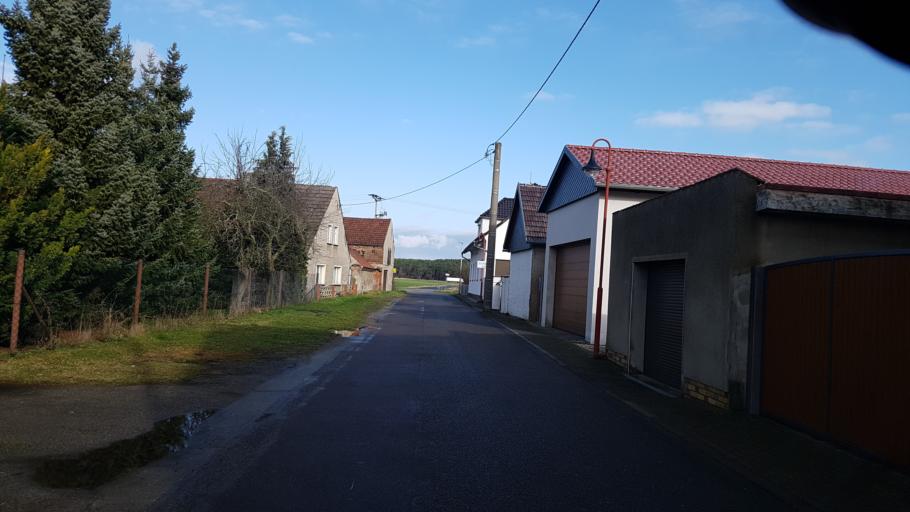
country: DE
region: Brandenburg
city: Schlieben
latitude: 51.7260
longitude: 13.3248
